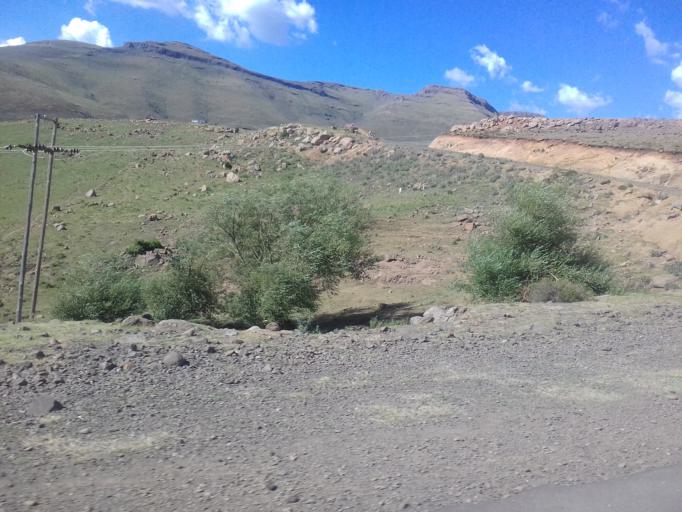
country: LS
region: Thaba-Tseka
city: Thaba-Tseka
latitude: -29.5141
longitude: 28.3228
